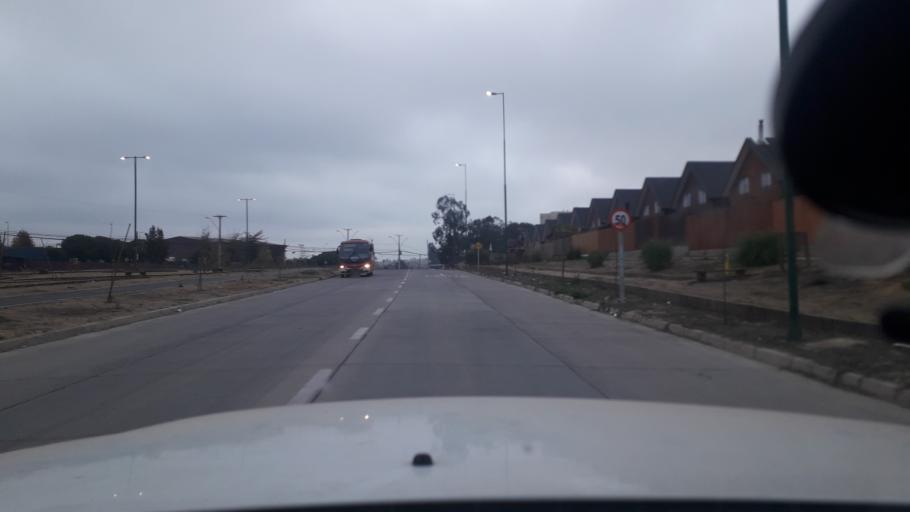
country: CL
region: Valparaiso
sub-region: Provincia de Valparaiso
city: Vina del Mar
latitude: -33.1266
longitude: -71.5693
